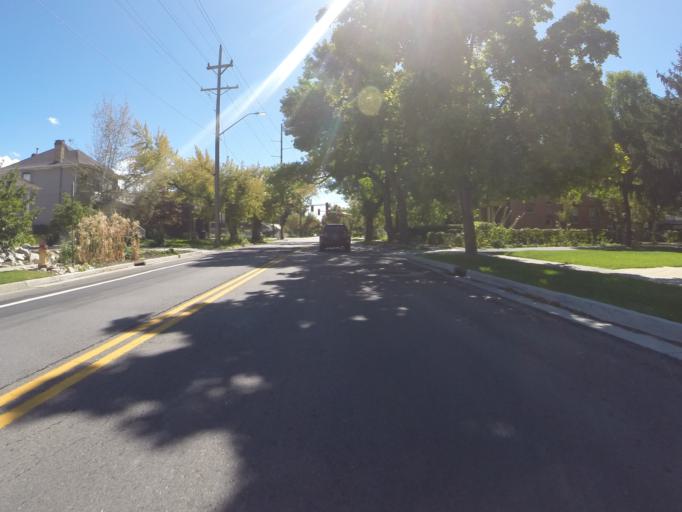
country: US
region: Utah
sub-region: Salt Lake County
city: South Salt Lake
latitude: 40.7344
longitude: -111.8768
